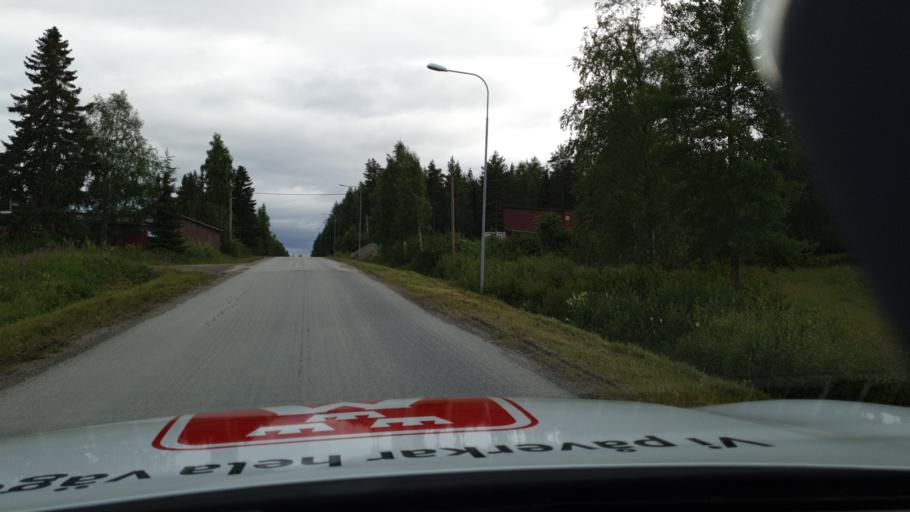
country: SE
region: Vaesterbotten
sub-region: Dorotea Kommun
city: Dorotea
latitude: 63.7989
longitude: 16.3990
